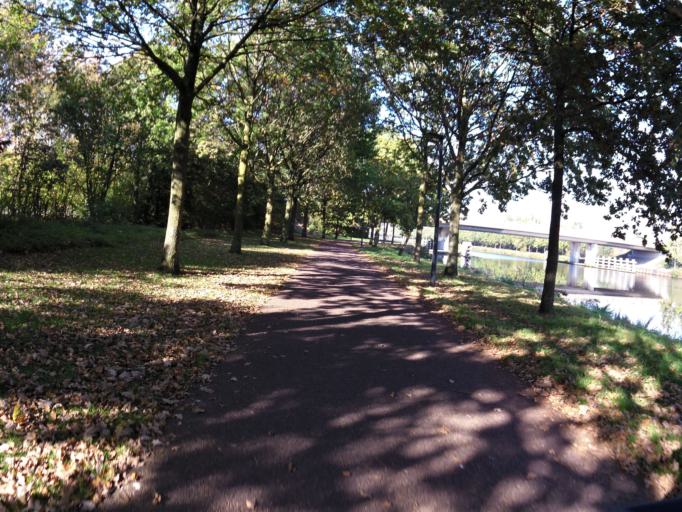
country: NL
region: North Brabant
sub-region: Gemeente Helmond
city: Helmond
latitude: 51.4886
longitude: 5.6819
